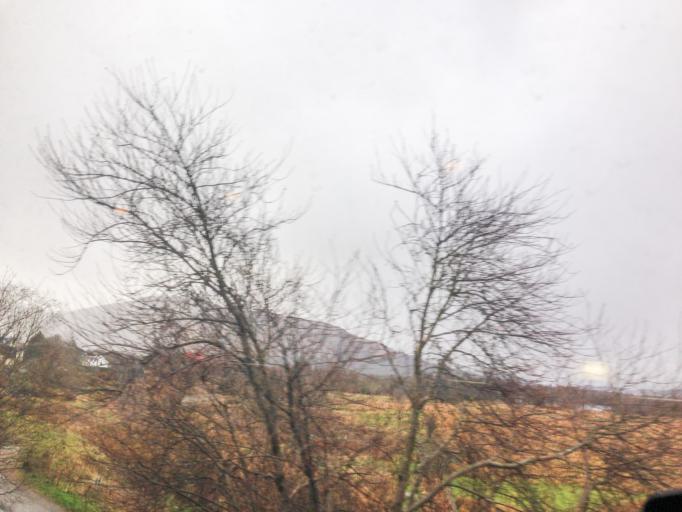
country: GB
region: Scotland
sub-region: Highland
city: Fort William
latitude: 56.8288
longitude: -5.0871
